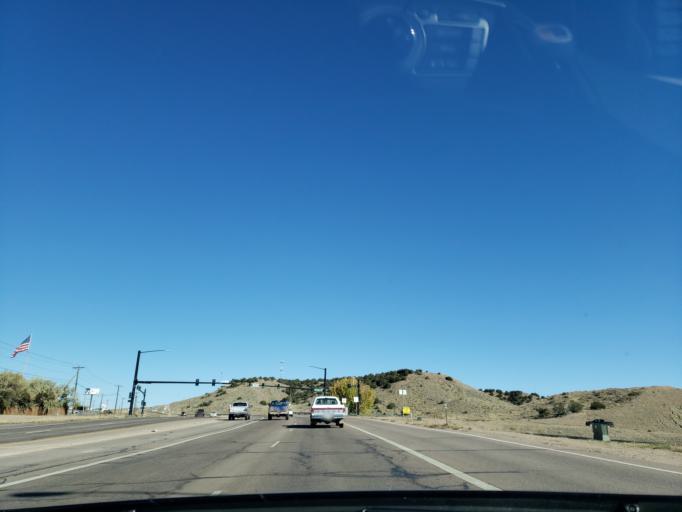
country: US
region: Colorado
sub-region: Fremont County
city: Lincoln Park
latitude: 38.4470
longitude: -105.1789
